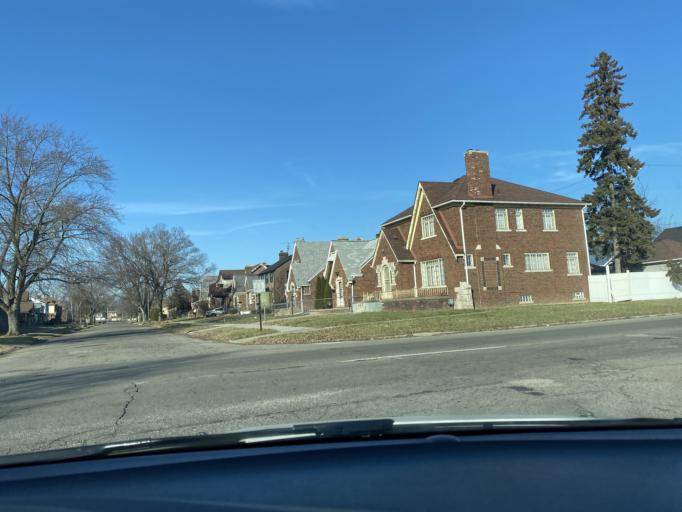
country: US
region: Michigan
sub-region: Wayne County
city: Grosse Pointe Park
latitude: 42.4059
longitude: -82.9470
